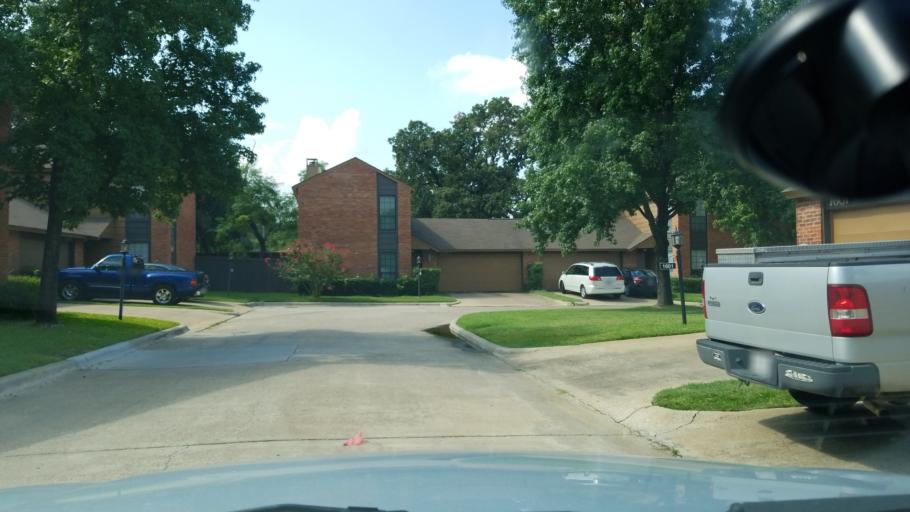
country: US
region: Texas
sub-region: Dallas County
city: Irving
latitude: 32.8337
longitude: -96.9252
